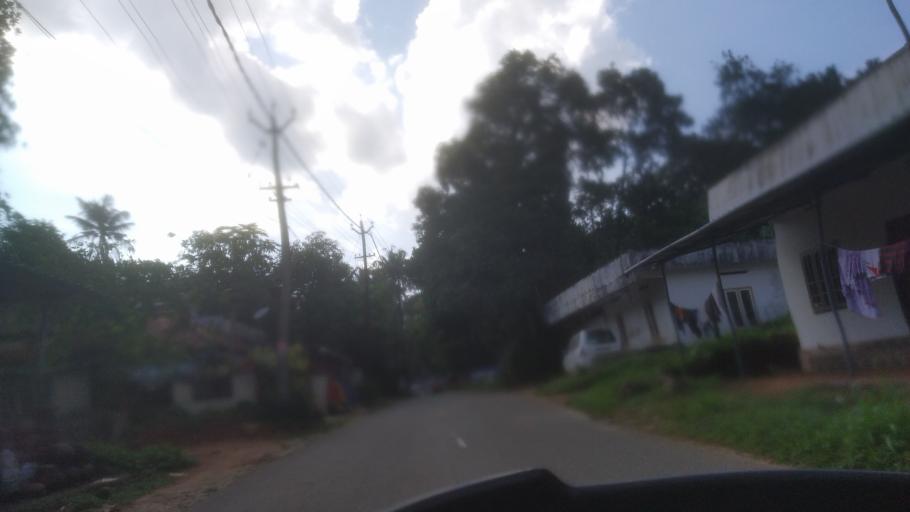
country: IN
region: Kerala
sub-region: Ernakulam
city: Muvattupula
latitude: 9.9960
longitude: 76.6101
